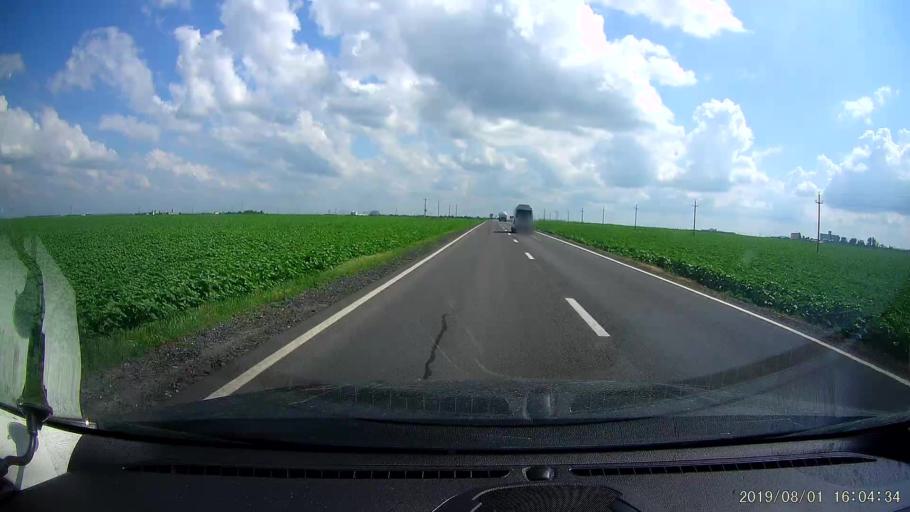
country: RO
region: Calarasi
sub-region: Comuna Dragalina
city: Drajna Noua
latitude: 44.4439
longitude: 27.3795
